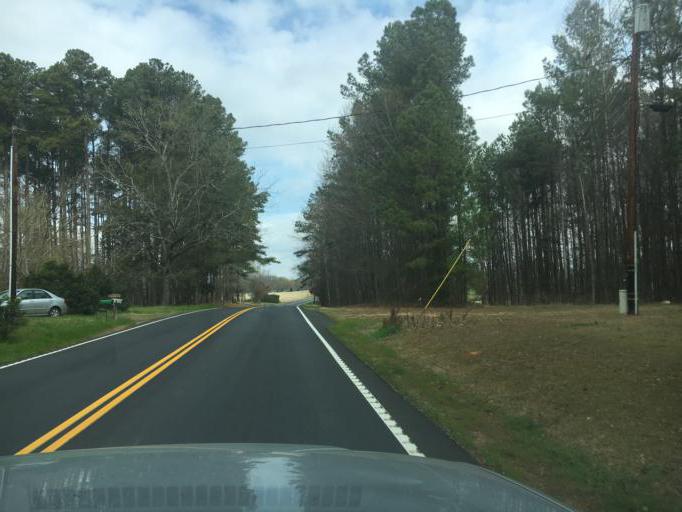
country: US
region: South Carolina
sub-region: Spartanburg County
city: Landrum
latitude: 35.1056
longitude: -82.2114
